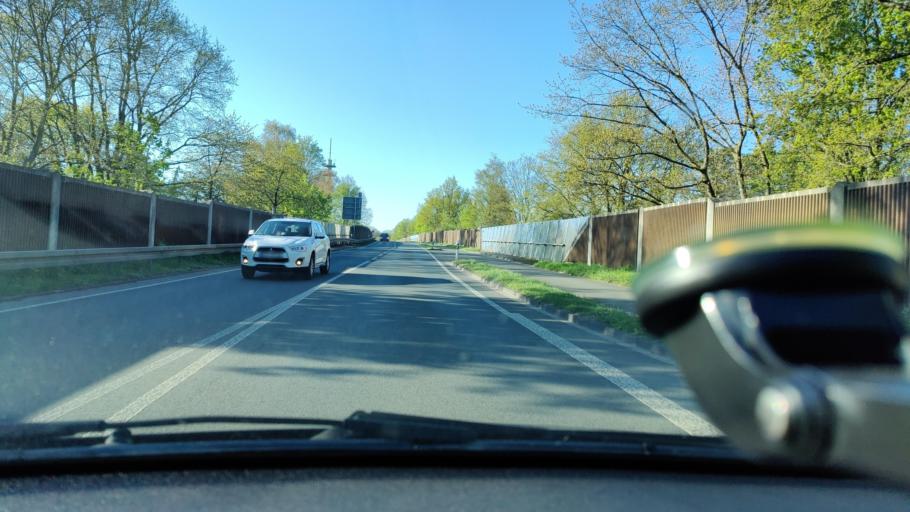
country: DE
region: North Rhine-Westphalia
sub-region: Regierungsbezirk Munster
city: Coesfeld
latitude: 51.9376
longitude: 7.1543
